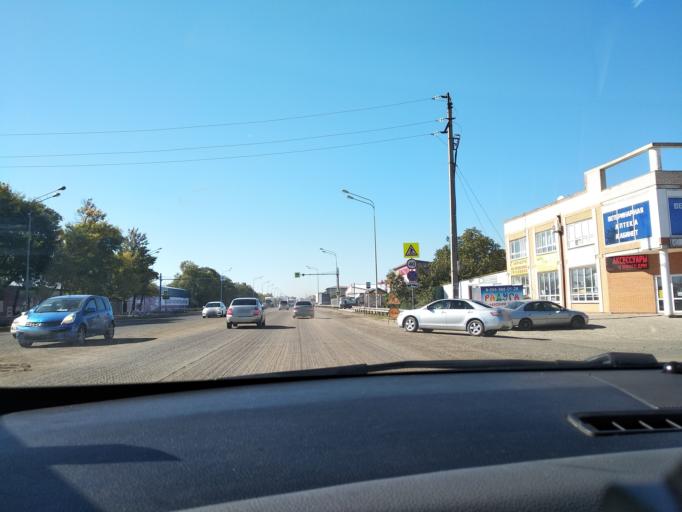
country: RU
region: Krasnodarskiy
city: Krasnodar
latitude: 45.1335
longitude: 39.0245
